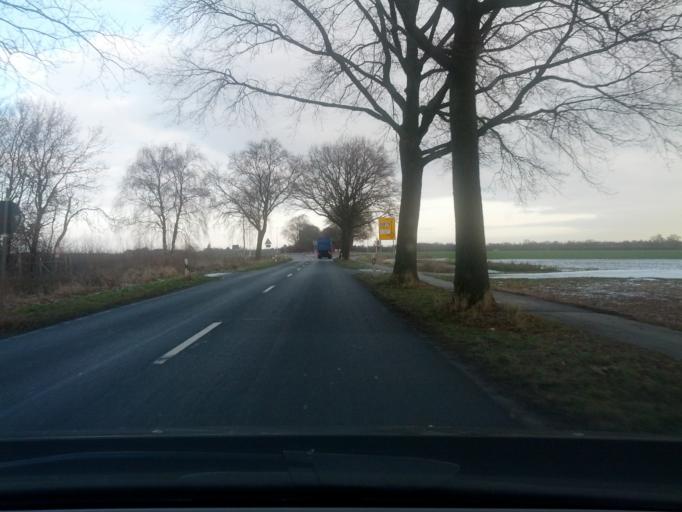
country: DE
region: Lower Saxony
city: Apensen
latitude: 53.4430
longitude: 9.6312
